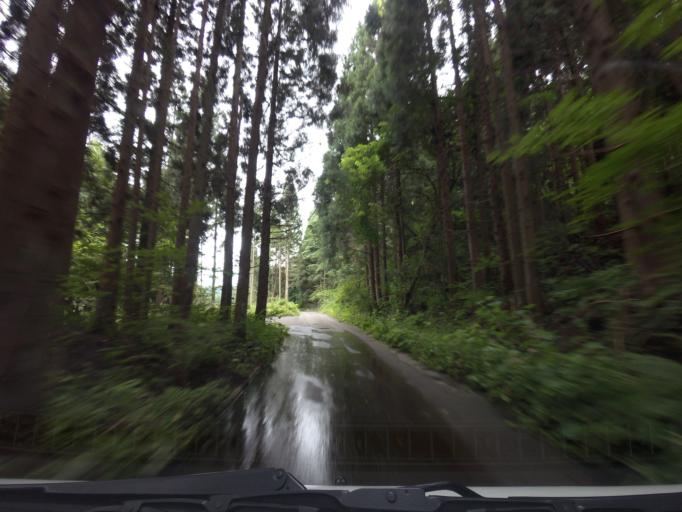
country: JP
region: Fukushima
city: Motomiya
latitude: 37.5552
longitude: 140.2976
